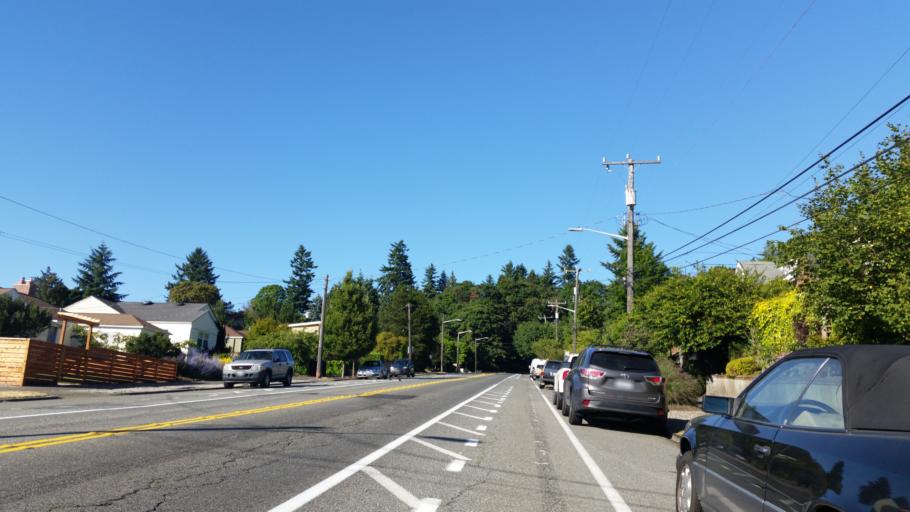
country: US
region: Washington
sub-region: King County
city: Seattle
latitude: 47.5781
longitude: -122.4018
